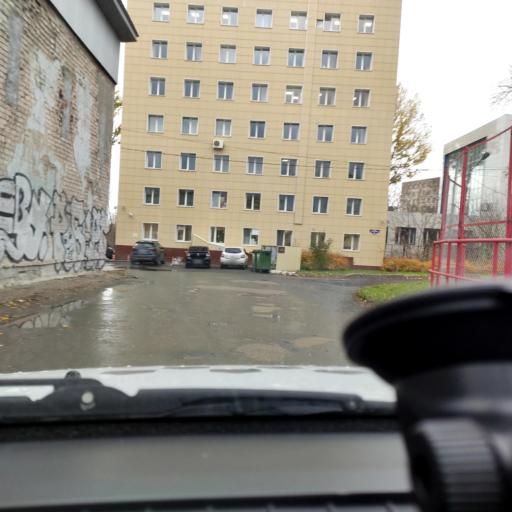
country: RU
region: Perm
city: Perm
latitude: 58.0023
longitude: 56.2840
